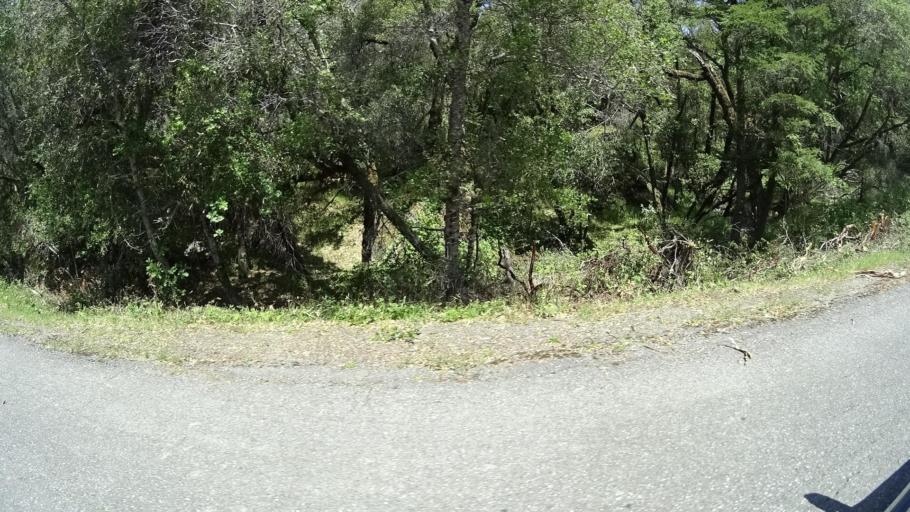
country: US
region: California
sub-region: Humboldt County
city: Redway
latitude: 40.2224
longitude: -123.6365
